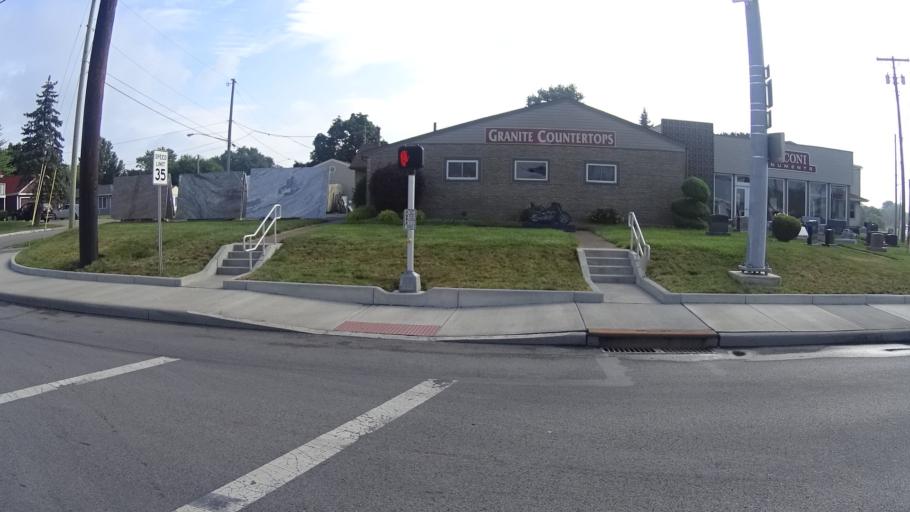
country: US
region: Ohio
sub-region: Erie County
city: Sandusky
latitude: 41.4328
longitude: -82.6884
